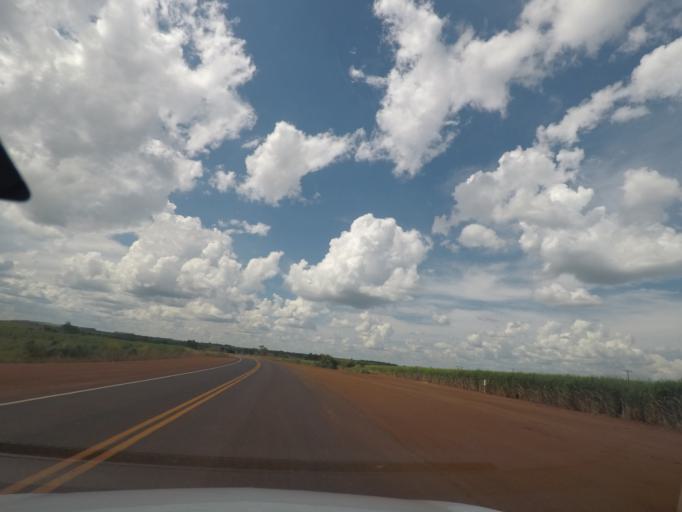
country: BR
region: Minas Gerais
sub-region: Conceicao Das Alagoas
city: Conceicao das Alagoas
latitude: -19.8055
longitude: -48.5807
